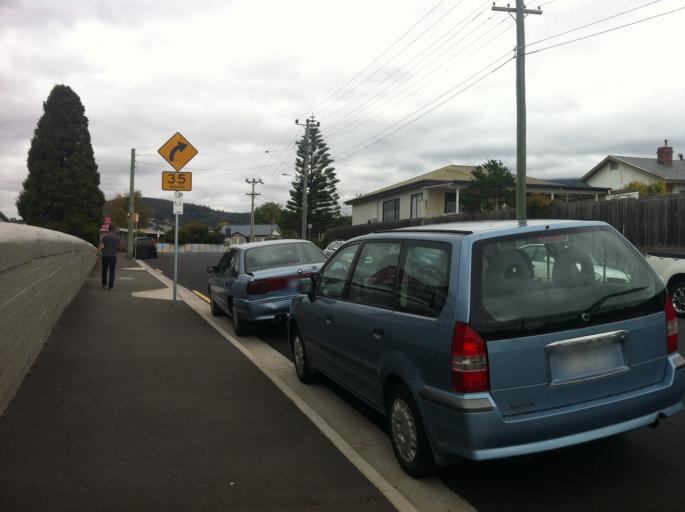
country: AU
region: Tasmania
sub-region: Glenorchy
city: Moonah
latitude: -42.8514
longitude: 147.3059
